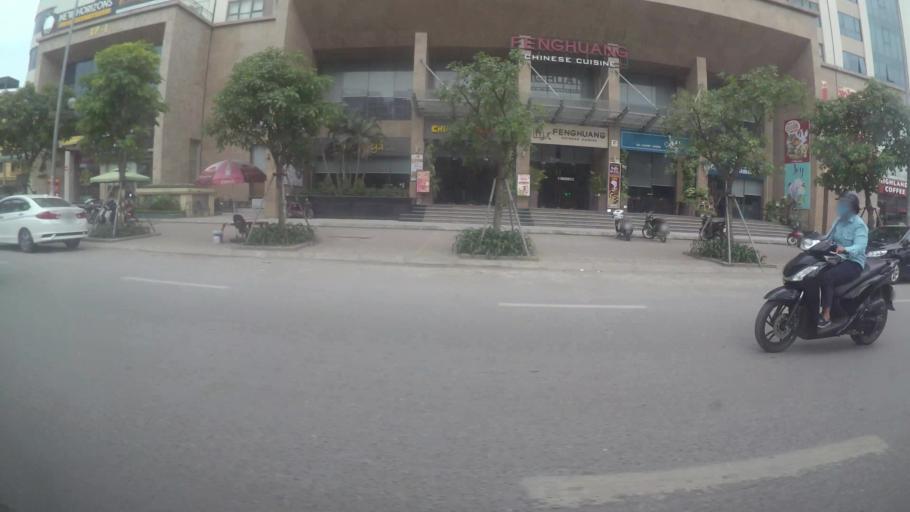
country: VN
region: Ha Noi
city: Cau Dien
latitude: 21.0342
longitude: 105.7701
